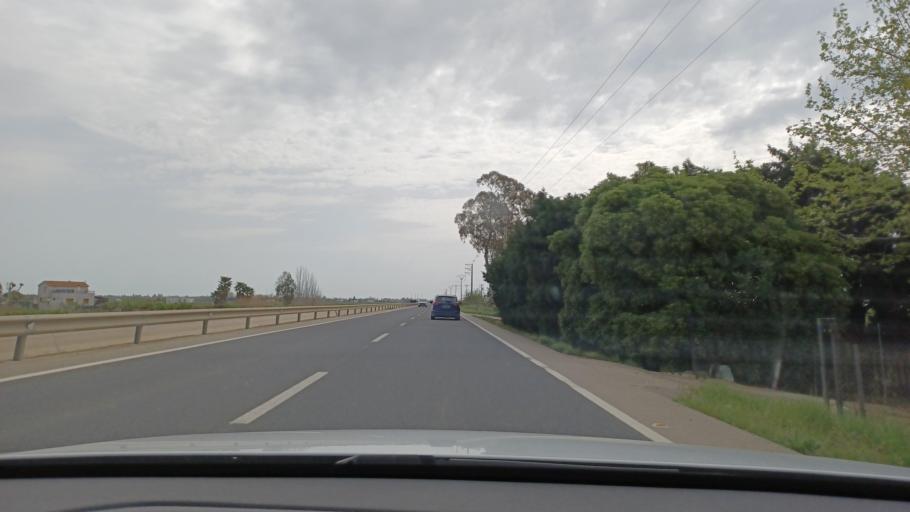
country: ES
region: Catalonia
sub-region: Provincia de Tarragona
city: Deltebre
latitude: 40.7101
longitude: 0.6563
